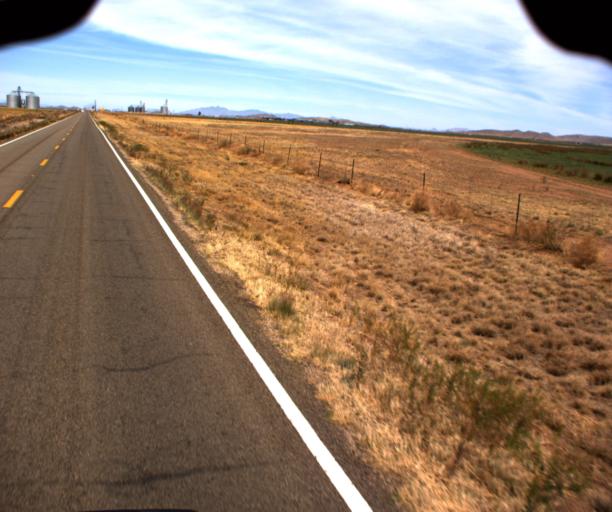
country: US
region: Arizona
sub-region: Cochise County
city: Tombstone
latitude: 31.7482
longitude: -109.6886
